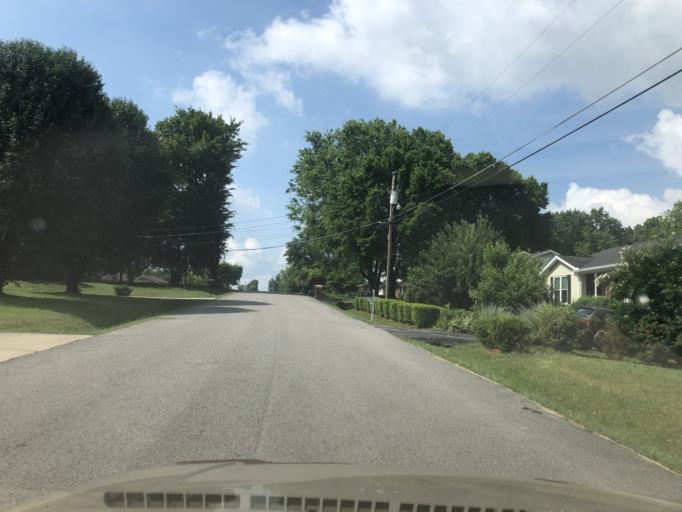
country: US
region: Tennessee
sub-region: Wilson County
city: Green Hill
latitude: 36.2385
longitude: -86.5887
